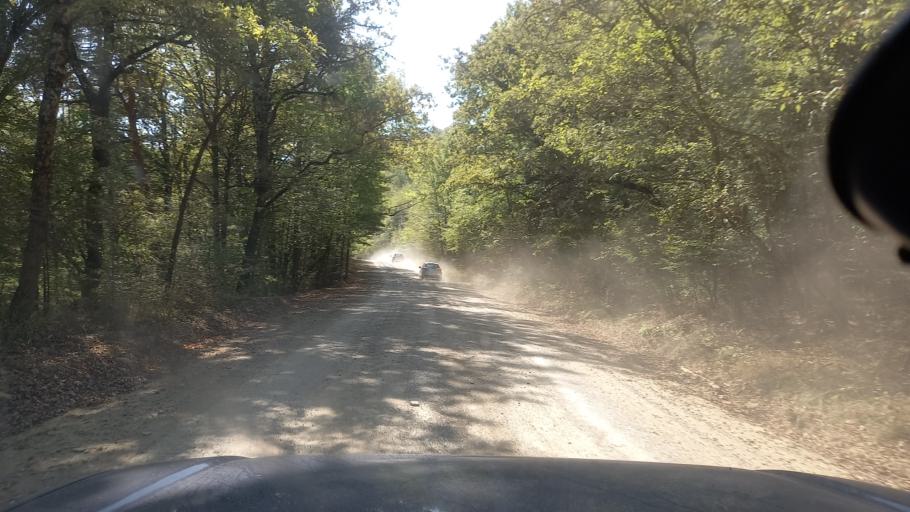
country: RU
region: Krasnodarskiy
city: Azovskaya
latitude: 44.6924
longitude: 38.6382
